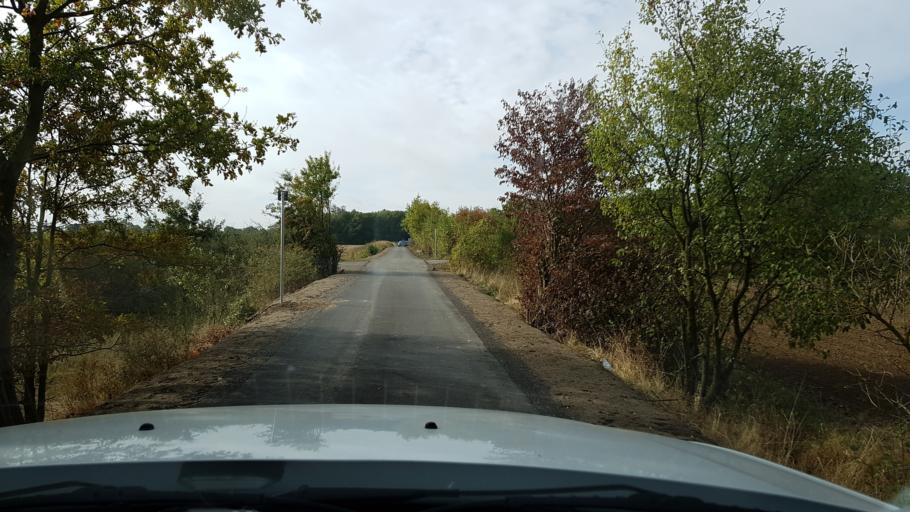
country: PL
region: West Pomeranian Voivodeship
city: Trzcinsko Zdroj
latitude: 52.9445
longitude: 14.5727
